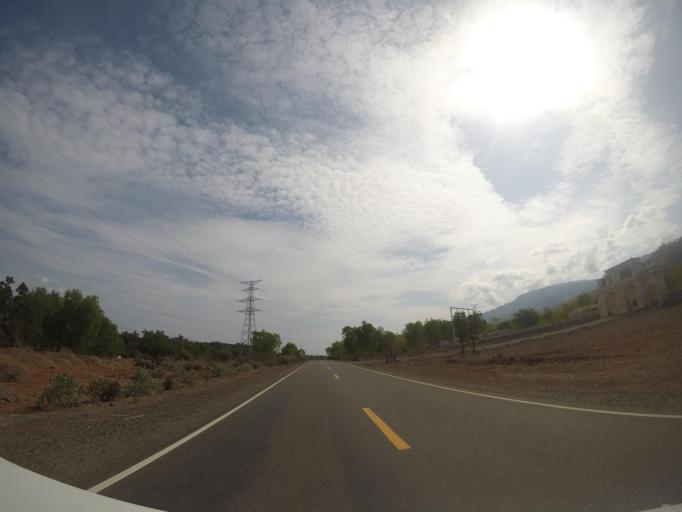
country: ID
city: Metinaro
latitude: -8.5028
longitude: 125.8120
